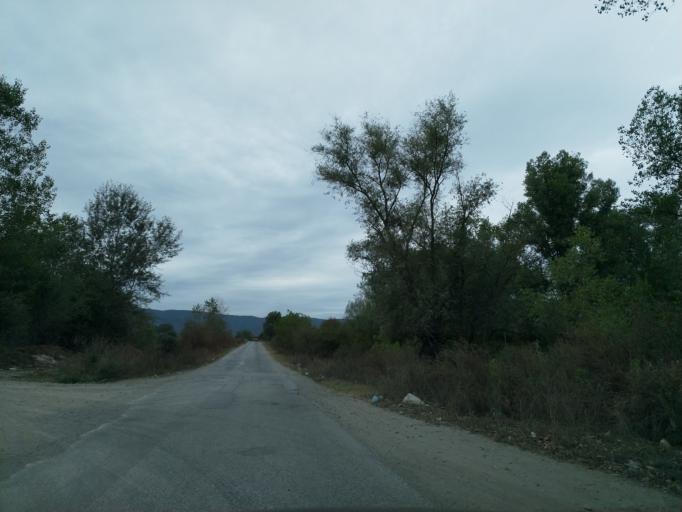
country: RS
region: Central Serbia
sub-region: Pomoravski Okrug
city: Paracin
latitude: 43.8270
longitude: 21.3492
